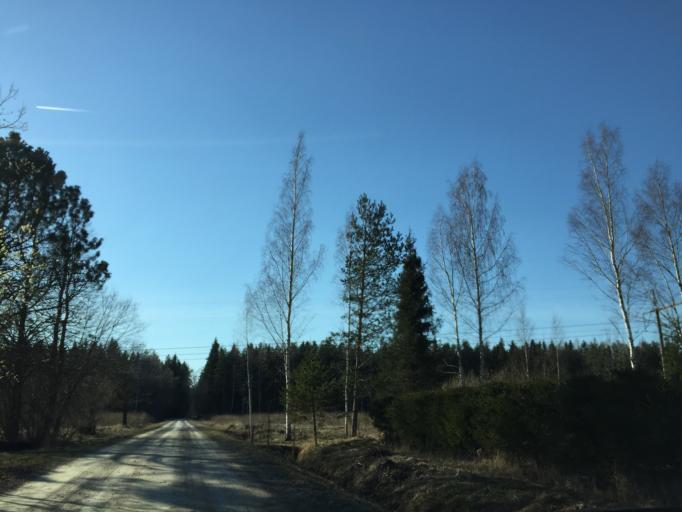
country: EE
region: Ida-Virumaa
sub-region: Sillamaee linn
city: Sillamae
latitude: 59.1408
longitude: 27.8164
